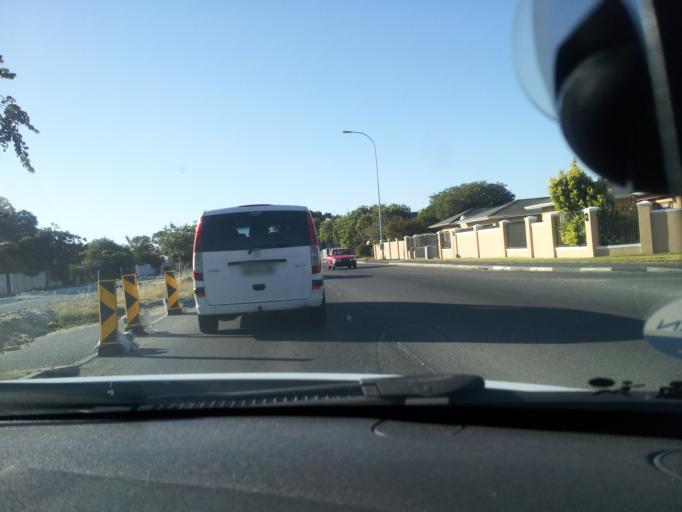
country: ZA
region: Western Cape
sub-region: Cape Winelands District Municipality
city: Stellenbosch
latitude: -34.1043
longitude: 18.8346
